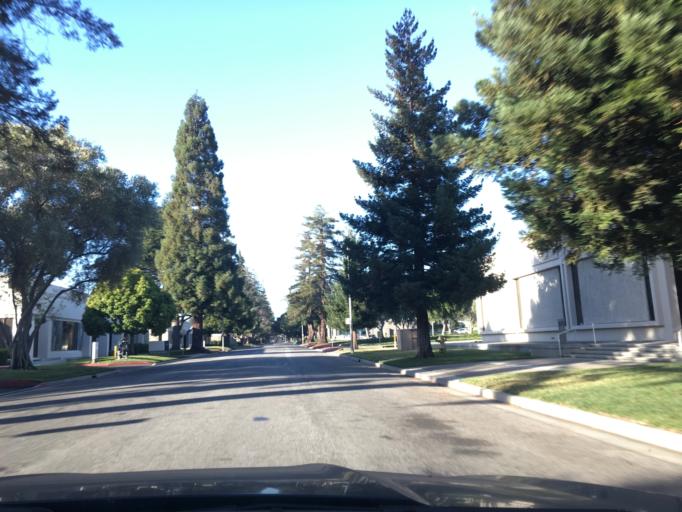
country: US
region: California
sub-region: Santa Clara County
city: Sunnyvale
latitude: 37.3973
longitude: -122.0338
